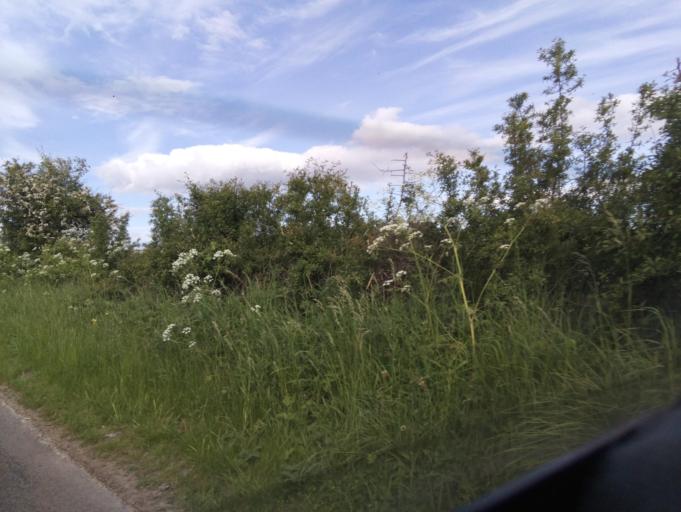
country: GB
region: England
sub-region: Gloucestershire
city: Donnington
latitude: 51.9616
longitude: -1.7603
